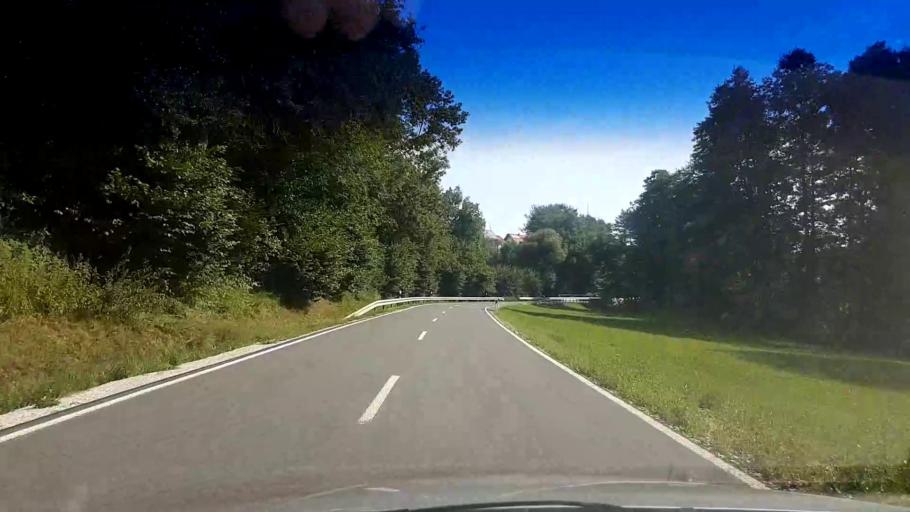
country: DE
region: Bavaria
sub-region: Upper Franconia
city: Glashutten
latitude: 49.9376
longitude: 11.3945
